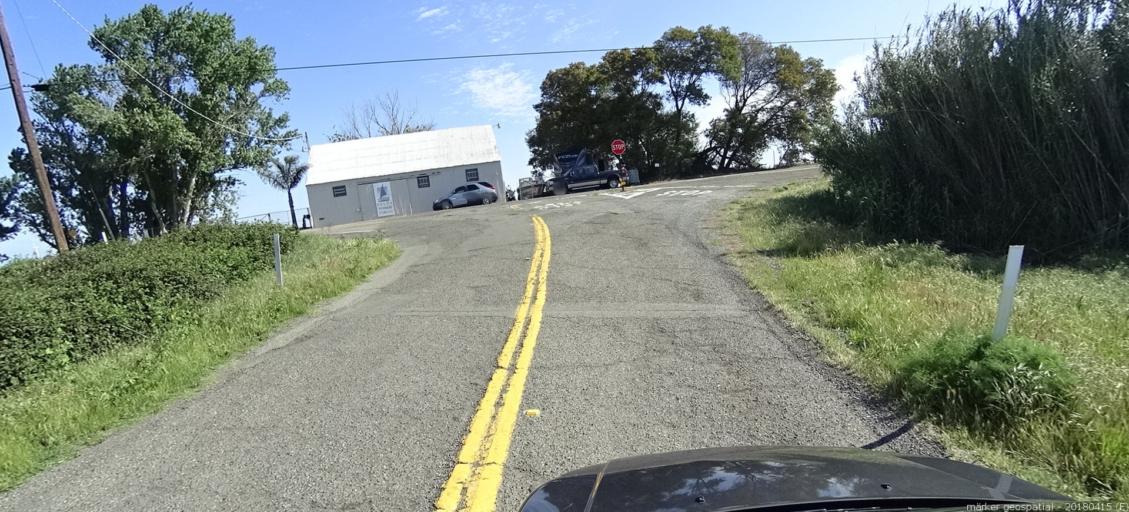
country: US
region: California
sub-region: Contra Costa County
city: Oakley
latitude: 38.0805
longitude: -121.7322
